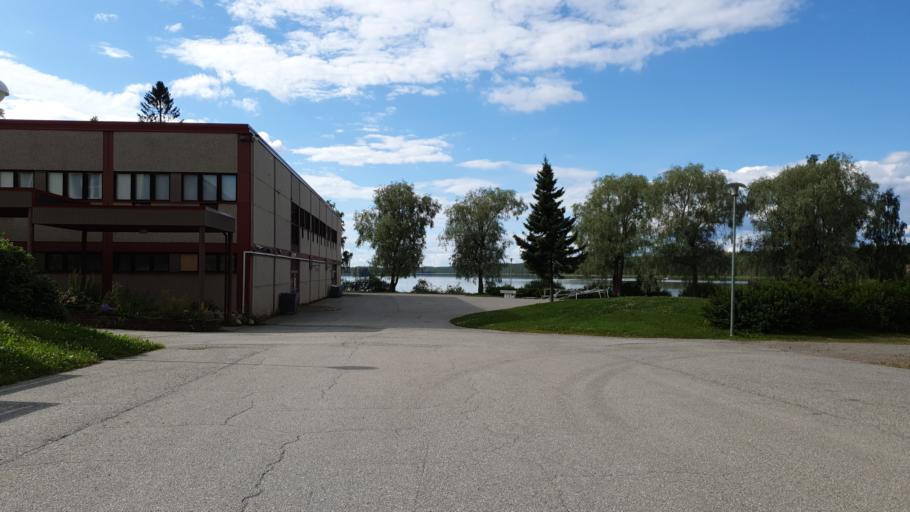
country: FI
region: Kainuu
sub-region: Kehys-Kainuu
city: Kuhmo
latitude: 64.1298
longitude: 29.5184
